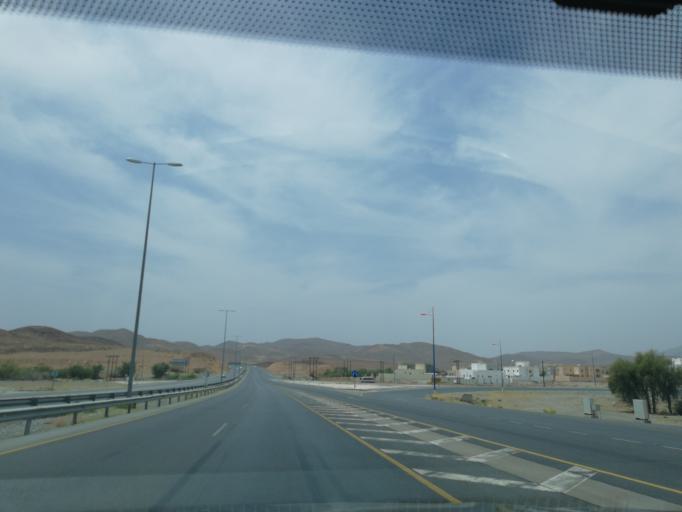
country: OM
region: Muhafazat ad Dakhiliyah
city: Izki
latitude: 22.9061
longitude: 57.7406
